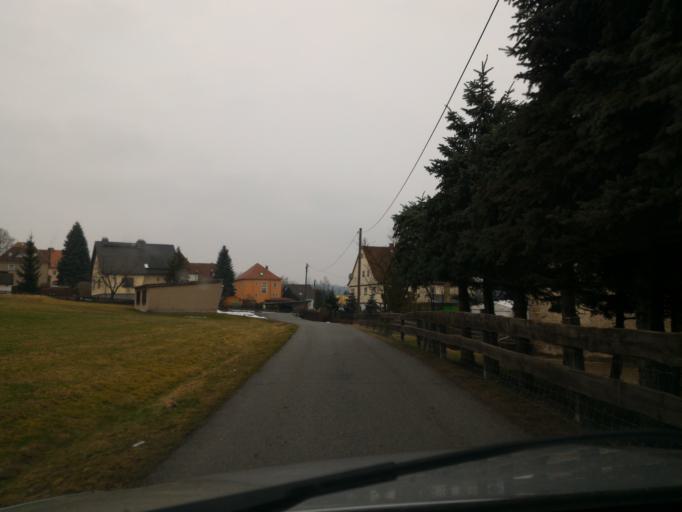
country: DE
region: Saxony
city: Seifhennersdorf
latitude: 50.9386
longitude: 14.6246
